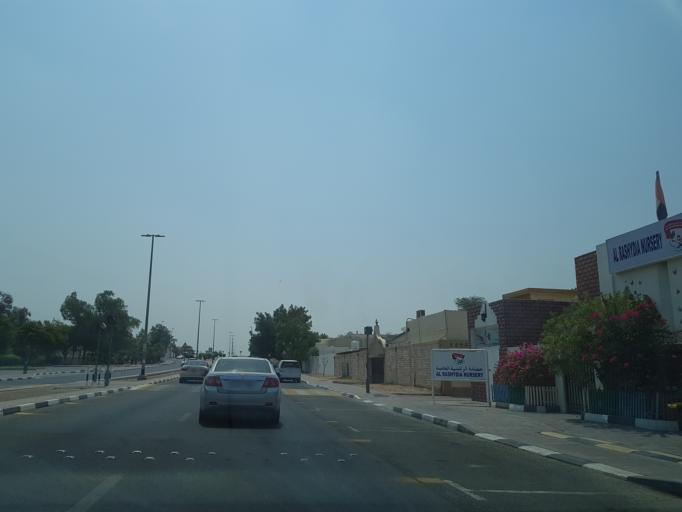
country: AE
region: Ash Shariqah
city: Sharjah
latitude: 25.2281
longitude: 55.3937
